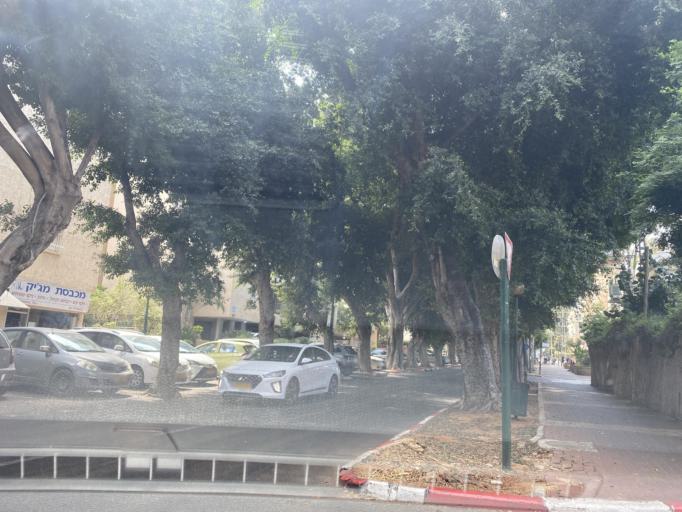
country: IL
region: Central District
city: Kfar Saba
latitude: 32.1738
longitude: 34.9080
